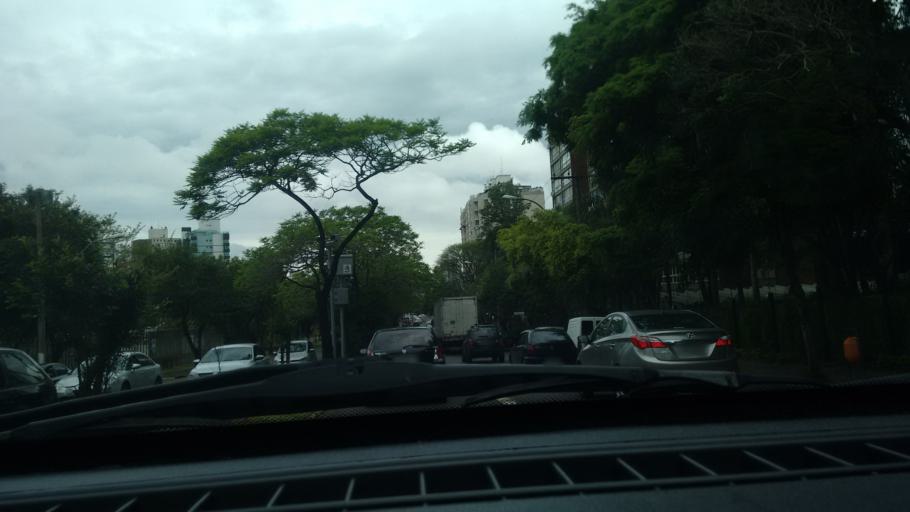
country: BR
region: Rio Grande do Sul
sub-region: Porto Alegre
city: Porto Alegre
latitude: -30.0326
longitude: -51.1844
